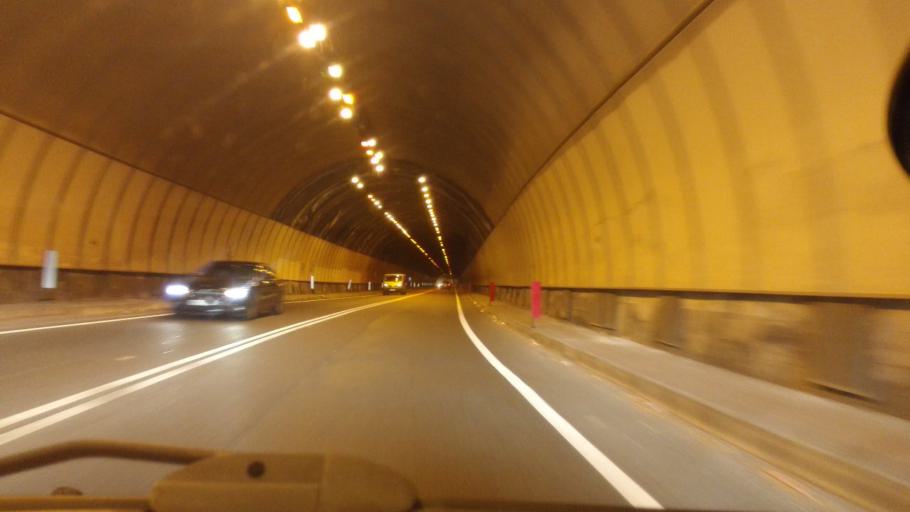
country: FR
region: Provence-Alpes-Cote d'Azur
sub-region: Departement des Alpes-Maritimes
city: Menton
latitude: 43.7849
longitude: 7.5329
